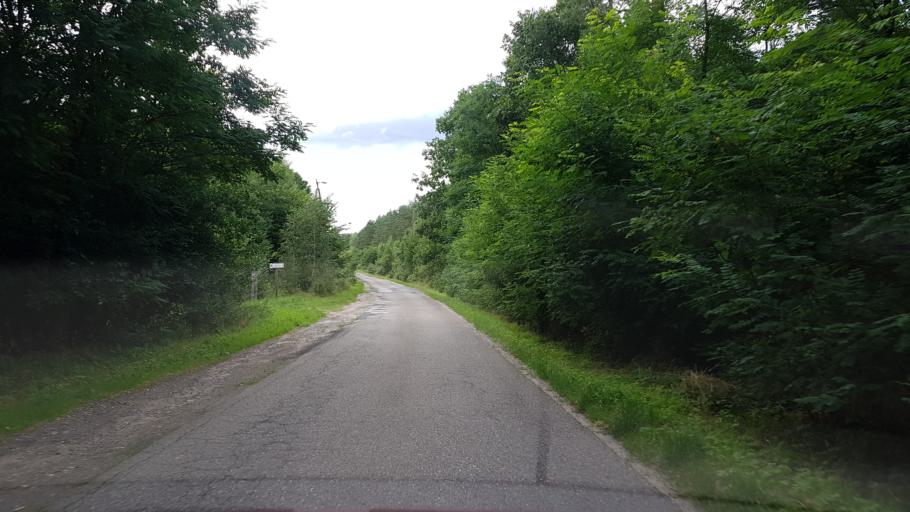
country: PL
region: West Pomeranian Voivodeship
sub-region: Powiat bialogardzki
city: Tychowo
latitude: 54.0283
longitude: 16.3536
